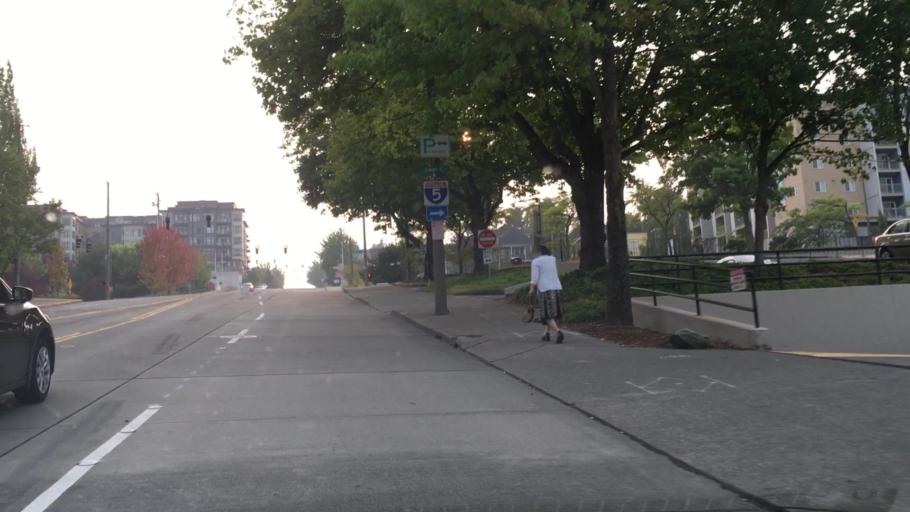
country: US
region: Washington
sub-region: Pierce County
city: Tacoma
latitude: 47.2491
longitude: -122.4397
